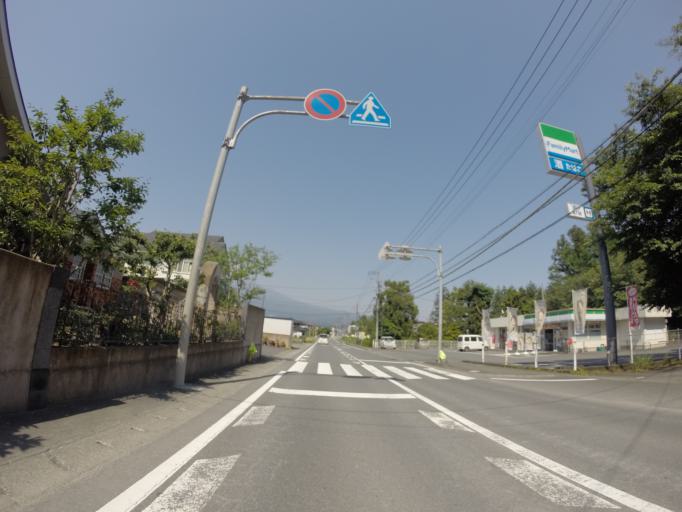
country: JP
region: Shizuoka
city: Fujinomiya
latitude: 35.2183
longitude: 138.5940
